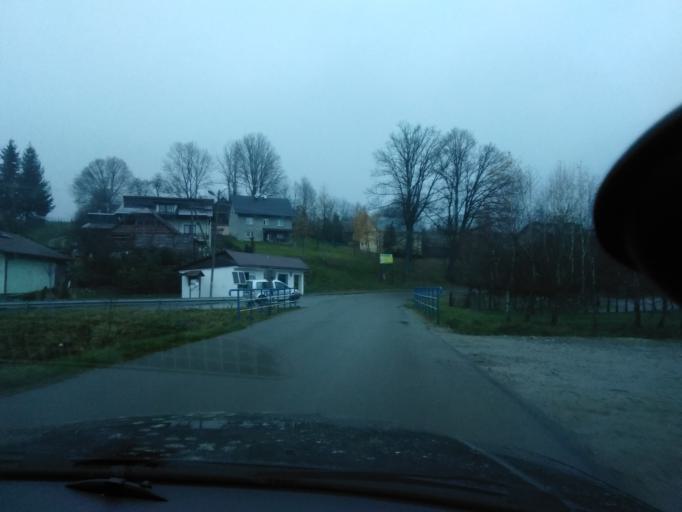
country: PL
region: Subcarpathian Voivodeship
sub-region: Powiat brzozowski
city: Wesola
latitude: 49.7512
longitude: 22.1146
